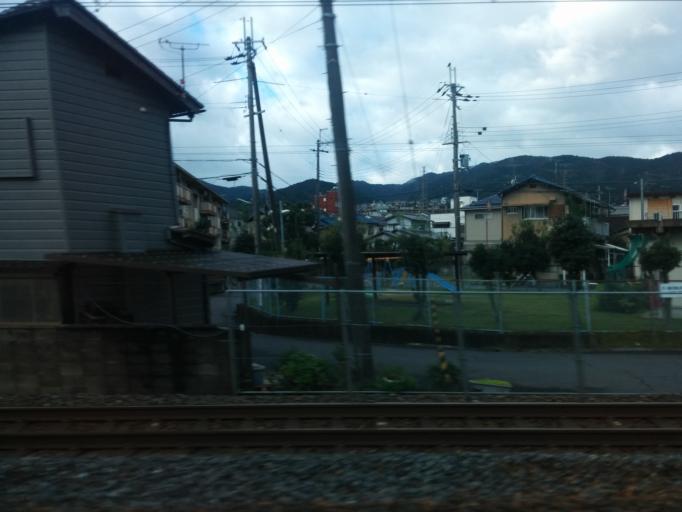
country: JP
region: Shiga Prefecture
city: Otsu-shi
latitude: 34.9877
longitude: 135.8897
